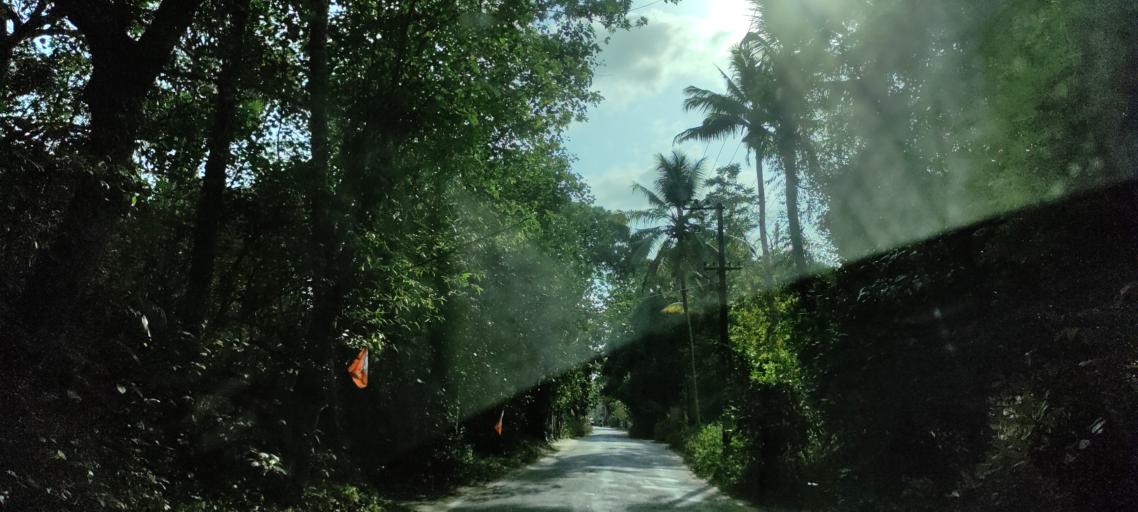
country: IN
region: Kerala
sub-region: Alappuzha
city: Vayalar
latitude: 9.6874
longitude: 76.3113
